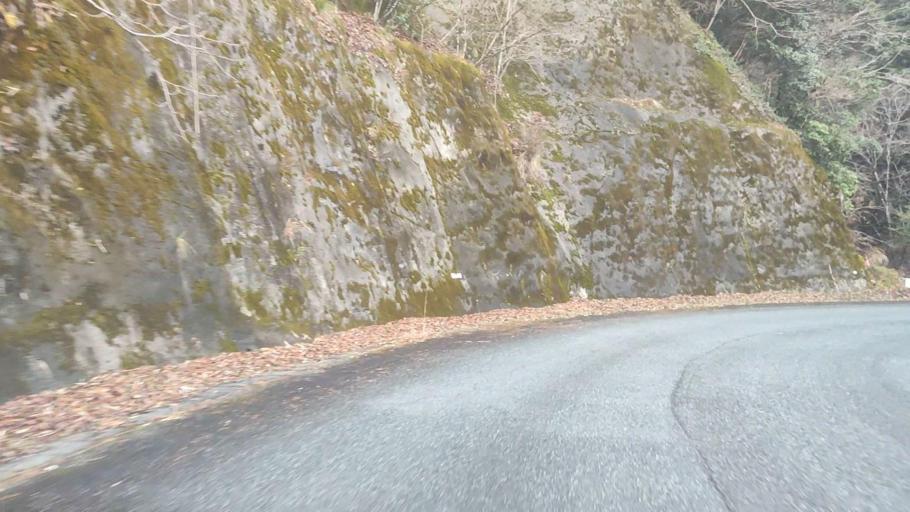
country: JP
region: Kumamoto
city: Matsubase
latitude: 32.4890
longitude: 130.9010
